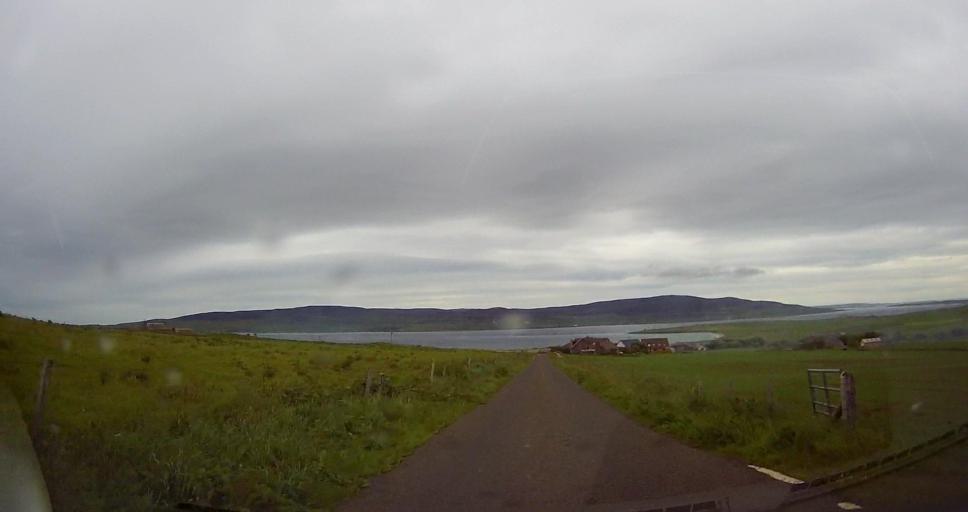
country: GB
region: Scotland
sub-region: Orkney Islands
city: Orkney
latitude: 59.1119
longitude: -3.1165
